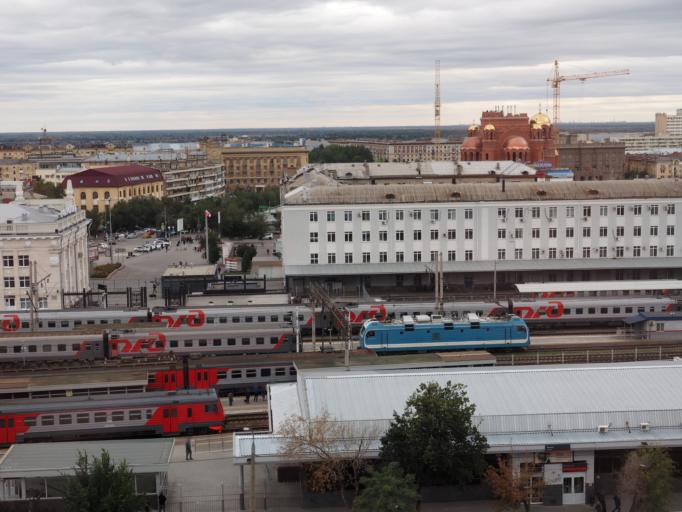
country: RU
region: Volgograd
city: Volgograd
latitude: 48.7132
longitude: 44.5115
